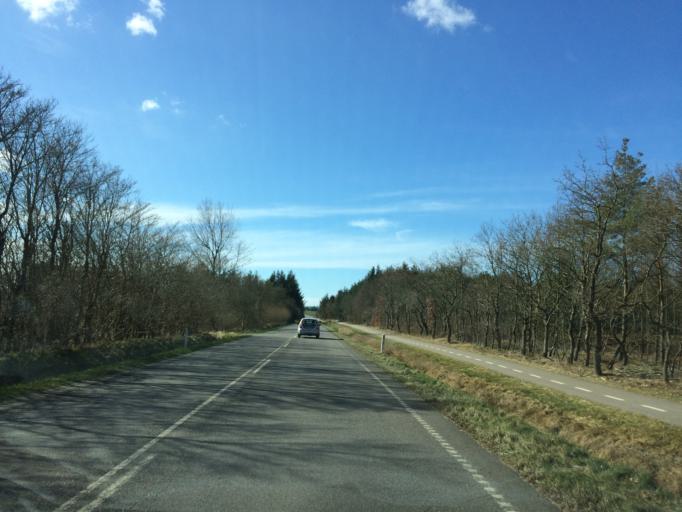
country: DK
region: South Denmark
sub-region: Varde Kommune
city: Oksbol
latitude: 55.7248
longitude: 8.2801
